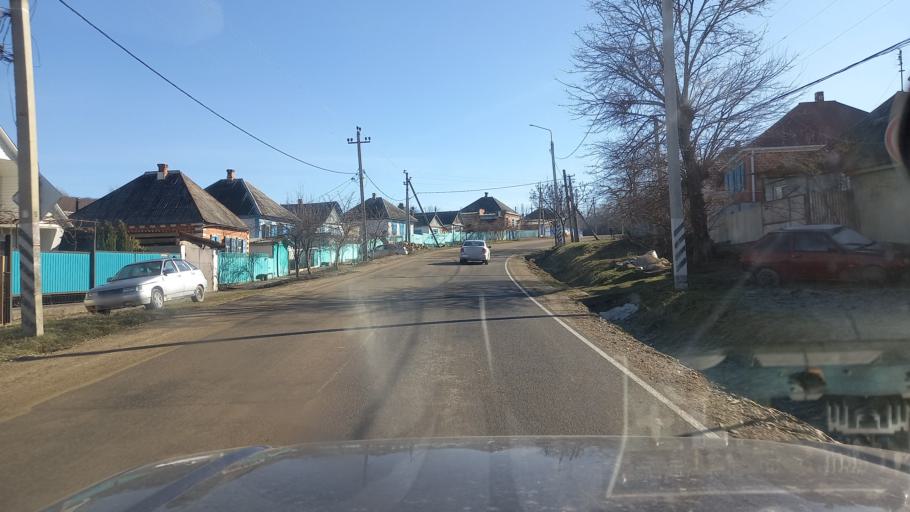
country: RU
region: Adygeya
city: Kamennomostskiy
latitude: 44.2909
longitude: 40.1992
